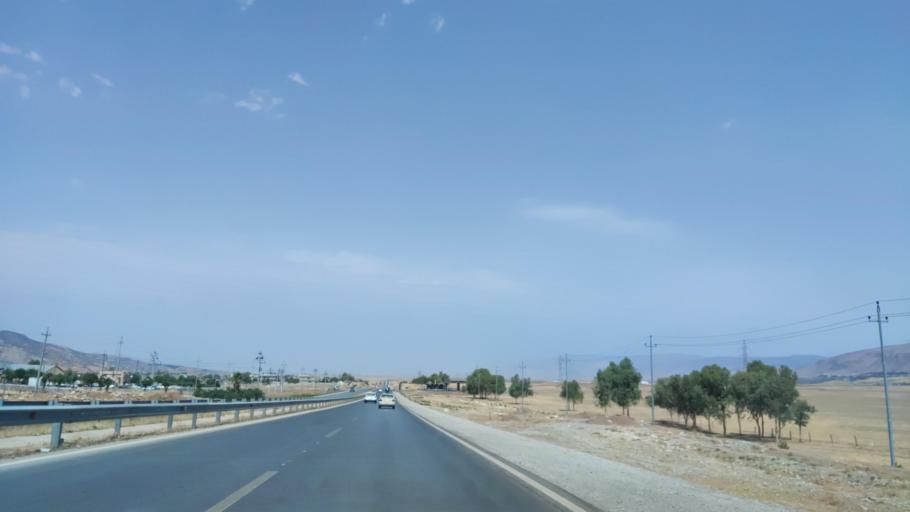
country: IQ
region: Arbil
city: Shaqlawah
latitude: 36.4965
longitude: 44.3648
